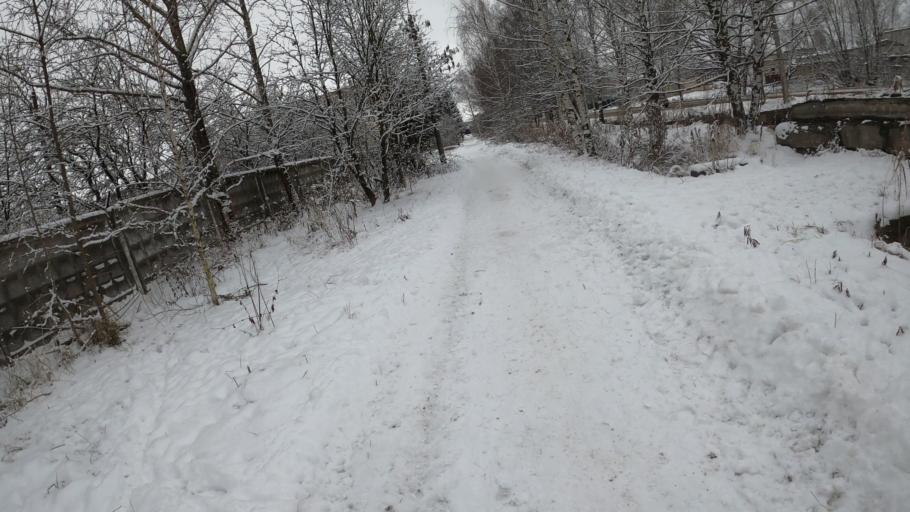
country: RU
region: Jaroslavl
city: Pereslavl'-Zalesskiy
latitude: 56.7394
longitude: 38.8943
